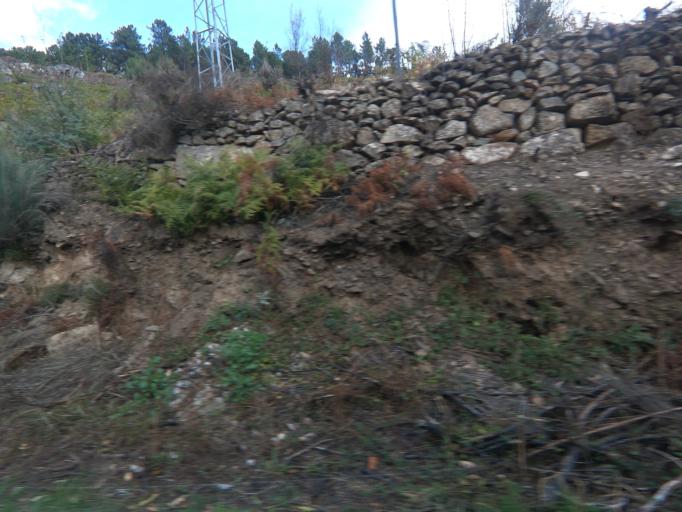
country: PT
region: Vila Real
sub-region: Vila Real
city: Vila Real
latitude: 41.3298
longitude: -7.7718
